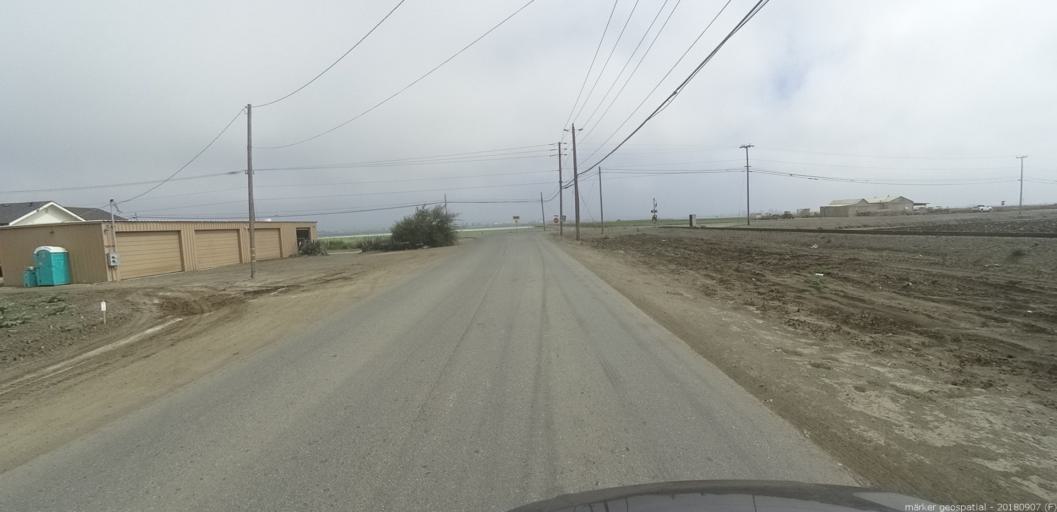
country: US
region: California
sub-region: Monterey County
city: Castroville
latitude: 36.7407
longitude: -121.7671
